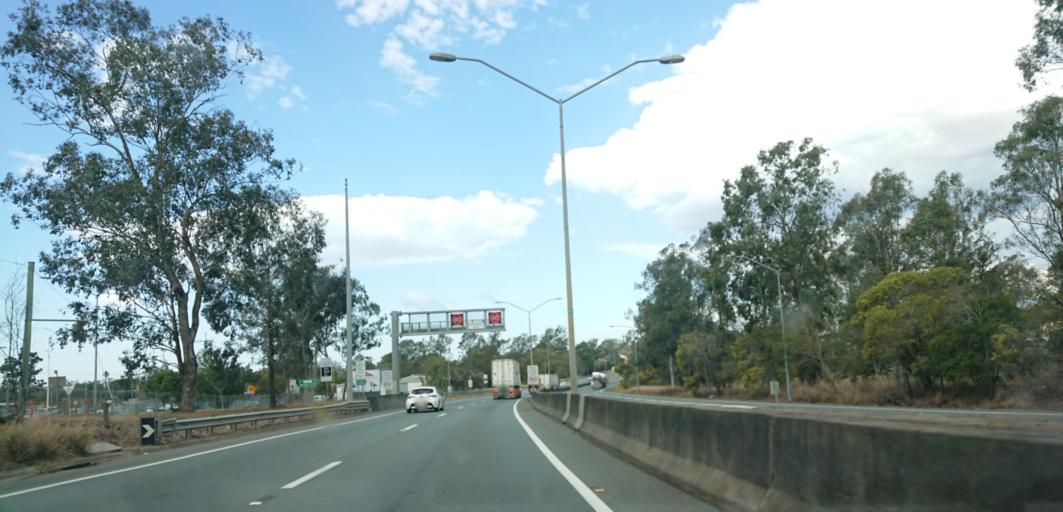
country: AU
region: Queensland
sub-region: Ipswich
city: Riverview
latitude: -27.5912
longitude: 152.8359
